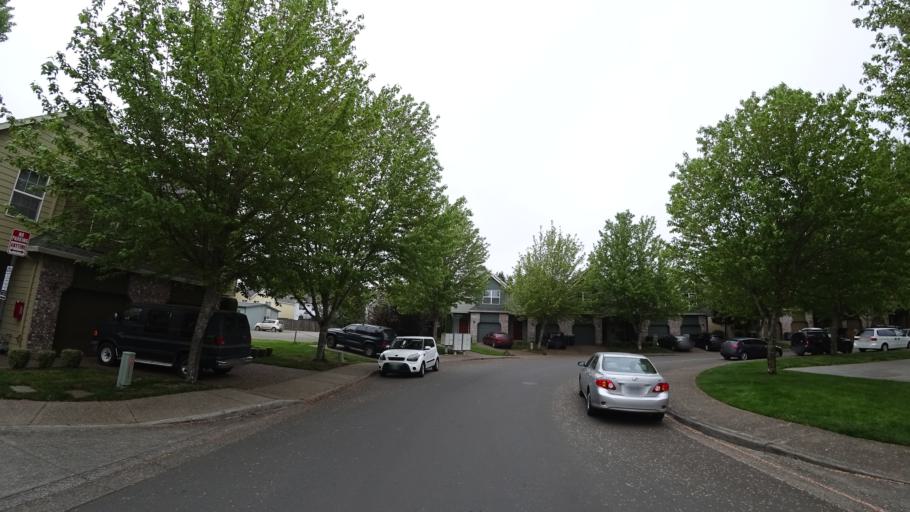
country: US
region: Oregon
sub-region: Washington County
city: Aloha
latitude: 45.5019
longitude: -122.8688
